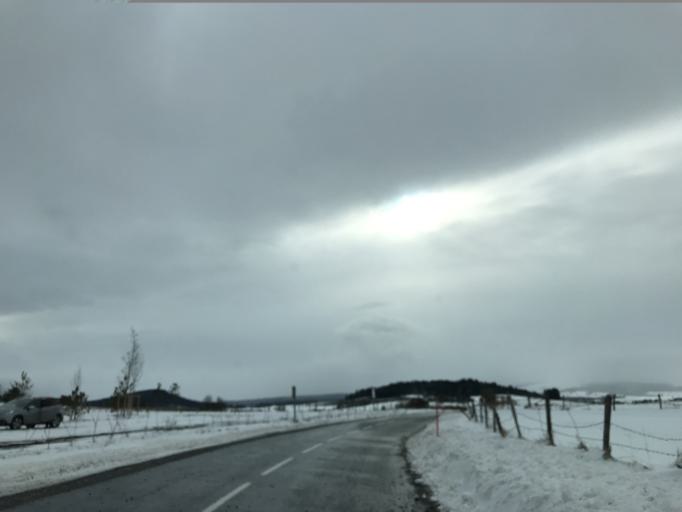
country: FR
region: Auvergne
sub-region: Departement du Puy-de-Dome
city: Aydat
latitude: 45.6692
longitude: 2.9386
